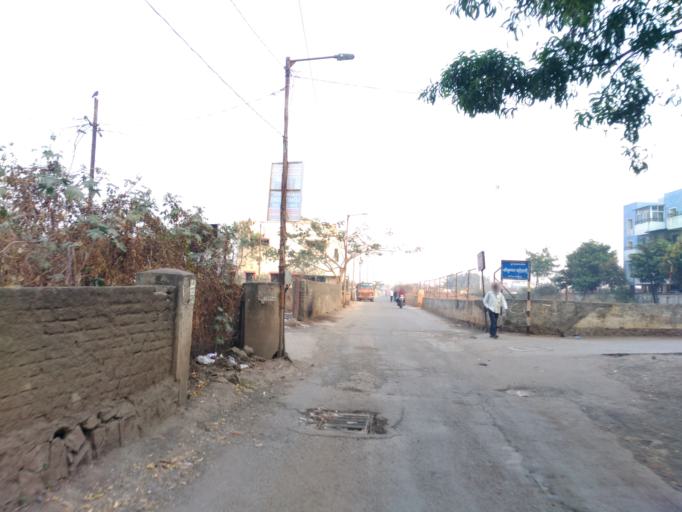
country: IN
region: Maharashtra
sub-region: Pune Division
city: Pune
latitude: 18.4576
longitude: 73.8730
